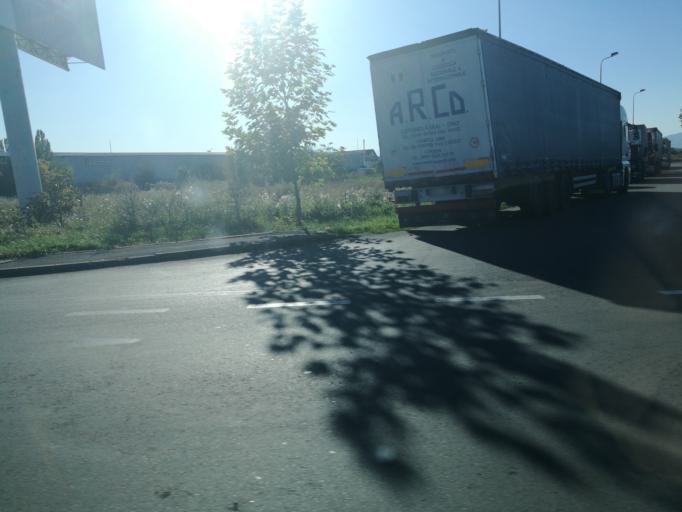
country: RO
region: Brasov
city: Brasov
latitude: 45.6836
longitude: 25.5838
